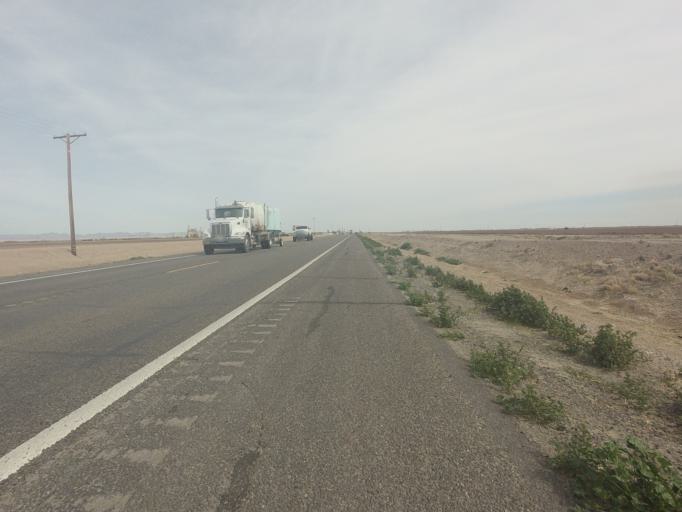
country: US
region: California
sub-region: Imperial County
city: Brawley
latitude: 32.9744
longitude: -115.4152
